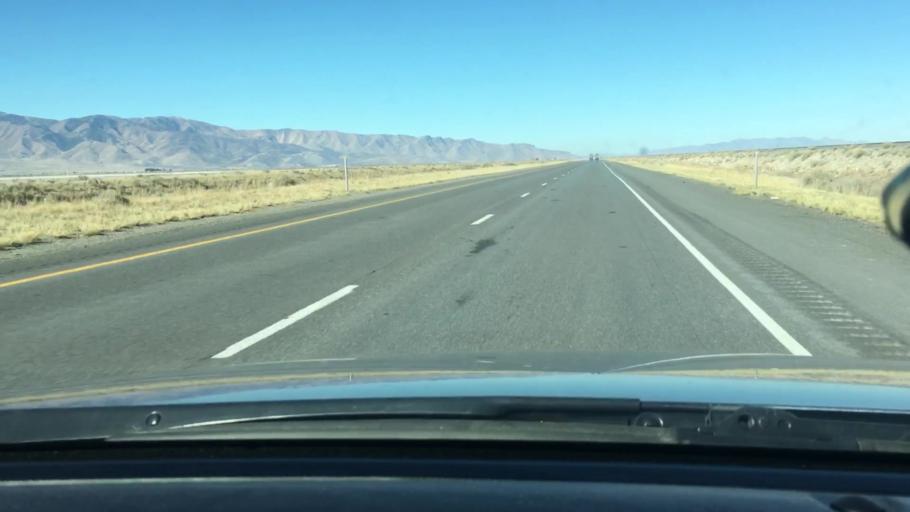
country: US
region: Utah
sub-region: Tooele County
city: Stansbury park
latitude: 40.6701
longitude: -112.3821
